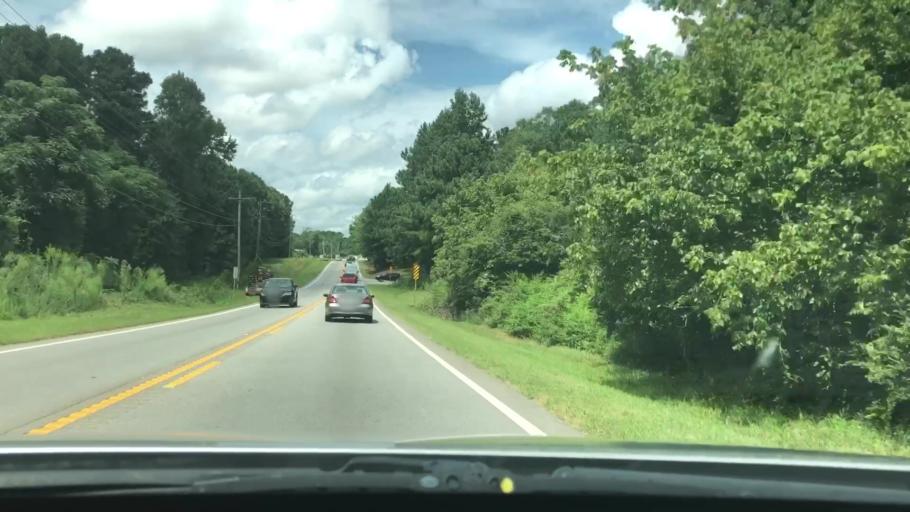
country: US
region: Georgia
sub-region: Henry County
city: Locust Grove
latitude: 33.3725
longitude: -84.1247
